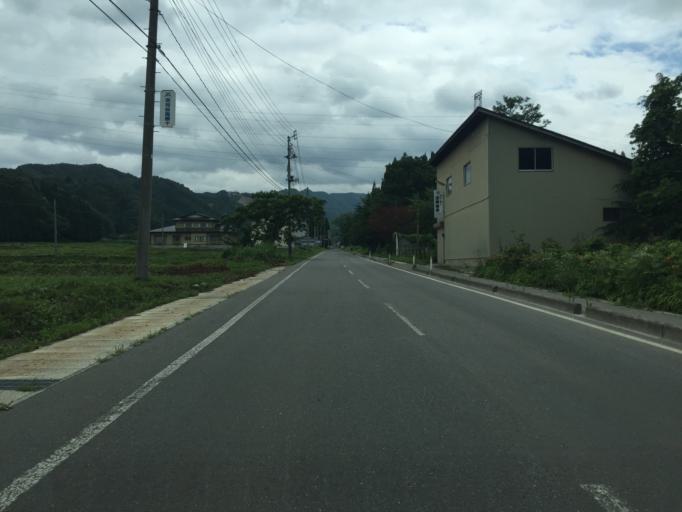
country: JP
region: Yamagata
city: Yonezawa
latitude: 37.8396
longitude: 140.0926
